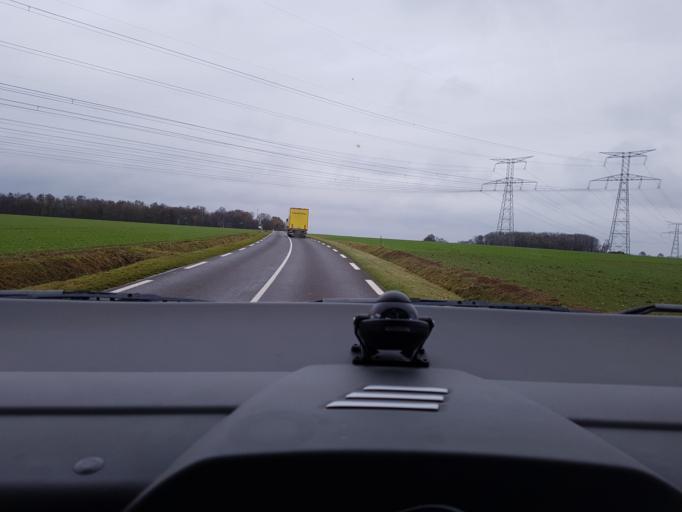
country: FR
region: Haute-Normandie
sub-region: Departement de la Seine-Maritime
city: Gournay-en-Bray
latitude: 49.4518
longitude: 1.6743
